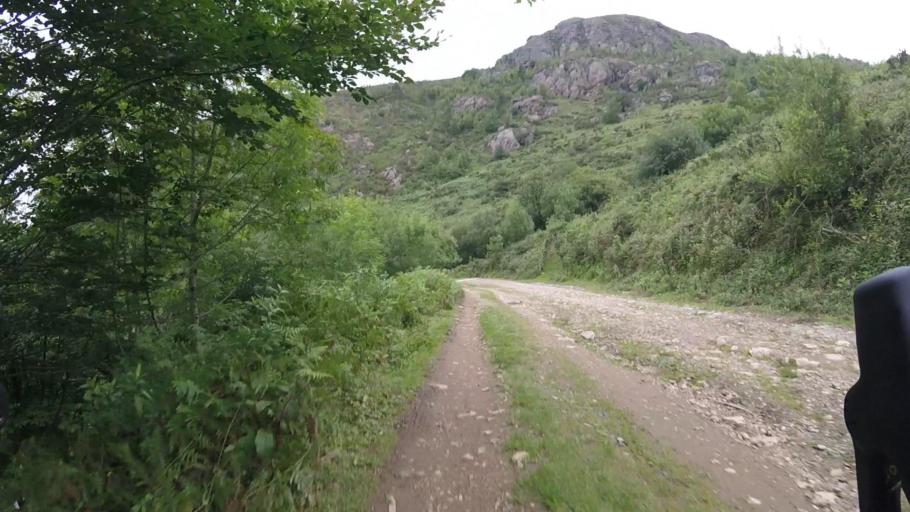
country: ES
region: Basque Country
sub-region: Provincia de Guipuzcoa
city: Irun
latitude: 43.2723
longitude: -1.7952
